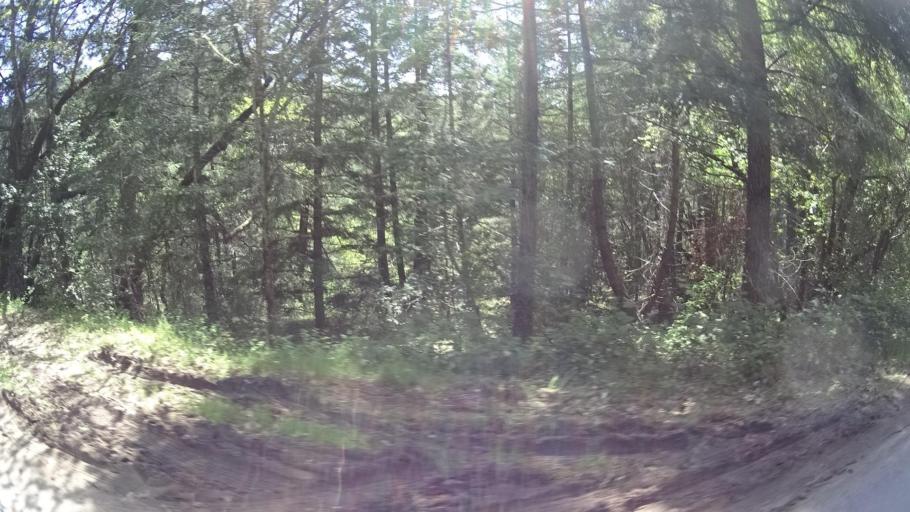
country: US
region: California
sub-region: Humboldt County
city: Redway
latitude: 40.1999
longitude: -123.5252
